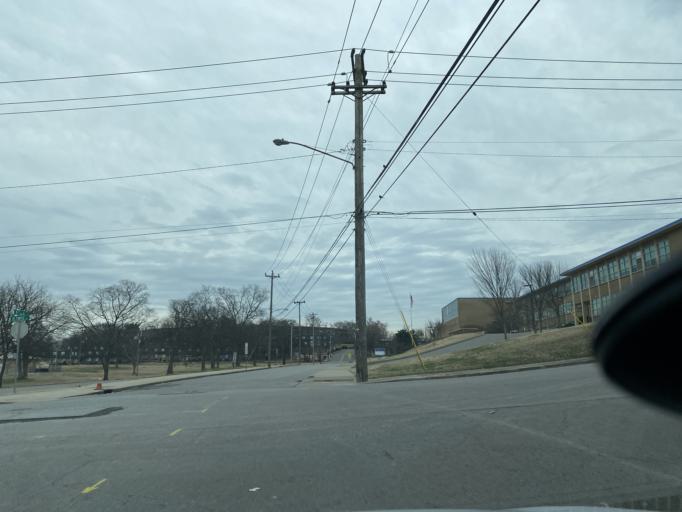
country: US
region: Tennessee
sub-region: Davidson County
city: Nashville
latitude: 36.1439
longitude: -86.7806
